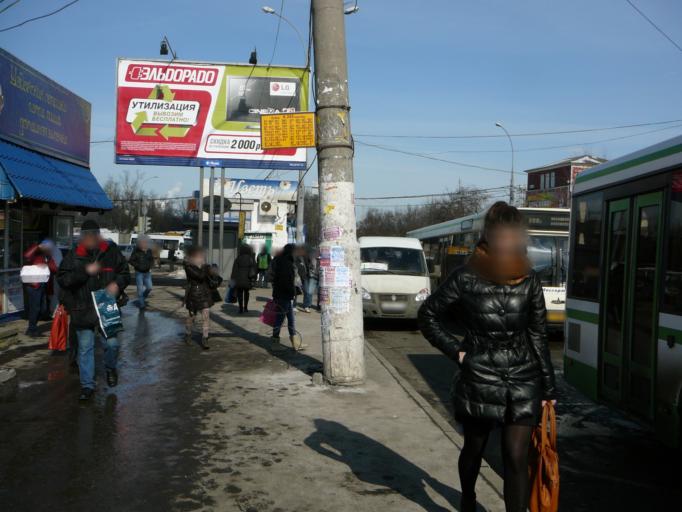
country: RU
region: Moscow
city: Orekhovo-Borisovo Severnoye
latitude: 55.6201
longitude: 37.6698
